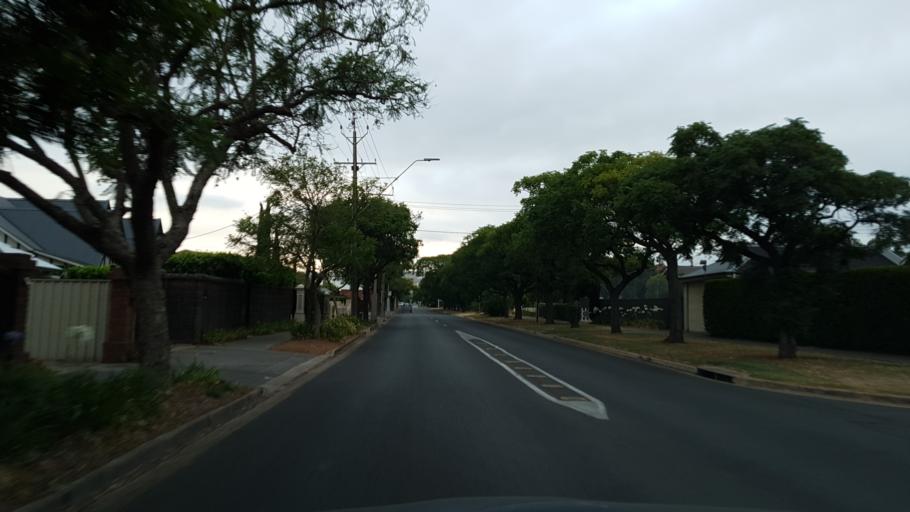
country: AU
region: South Australia
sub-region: Mitcham
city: Hawthorn
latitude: -34.9769
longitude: 138.5963
